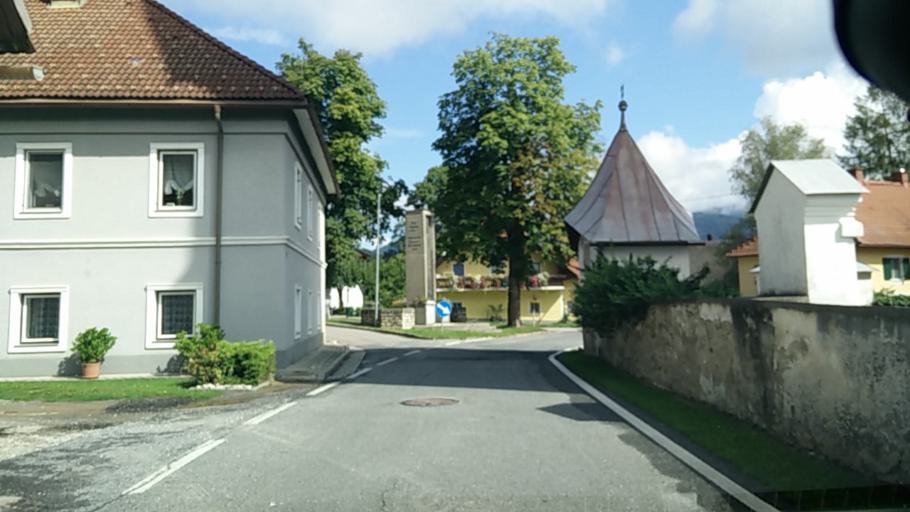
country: AT
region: Carinthia
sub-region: Politischer Bezirk Volkermarkt
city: Voelkermarkt
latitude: 46.6760
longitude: 14.5725
